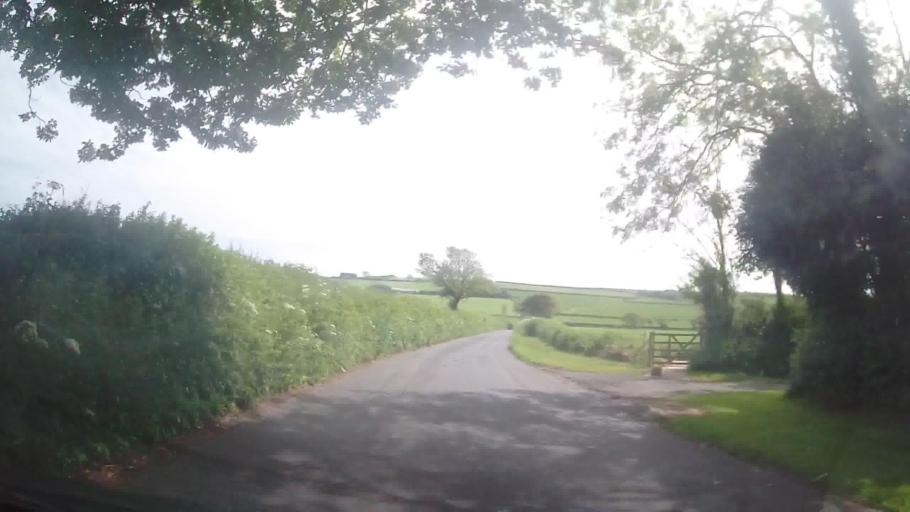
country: GB
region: England
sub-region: Devon
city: Salcombe
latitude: 50.2615
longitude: -3.6766
